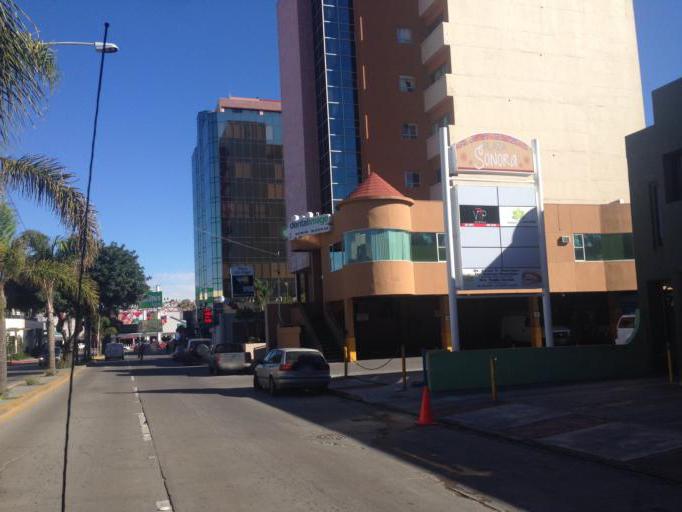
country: MX
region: Baja California
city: Tijuana
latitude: 32.5132
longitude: -117.0121
